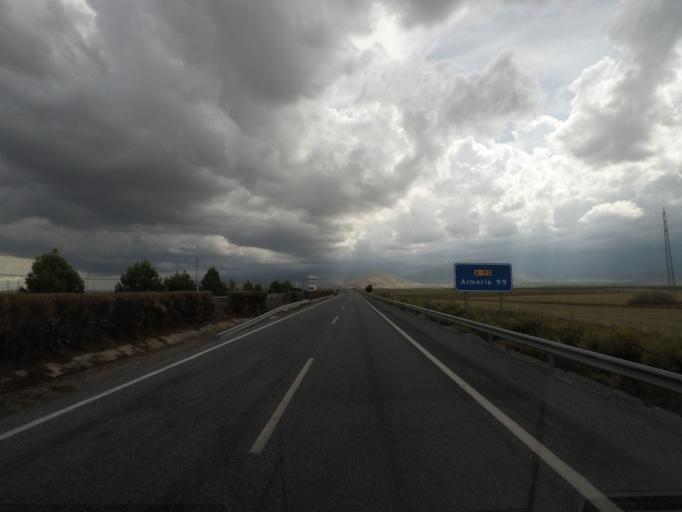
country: ES
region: Andalusia
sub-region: Provincia de Granada
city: Albunan
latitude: 37.2244
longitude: -3.0798
